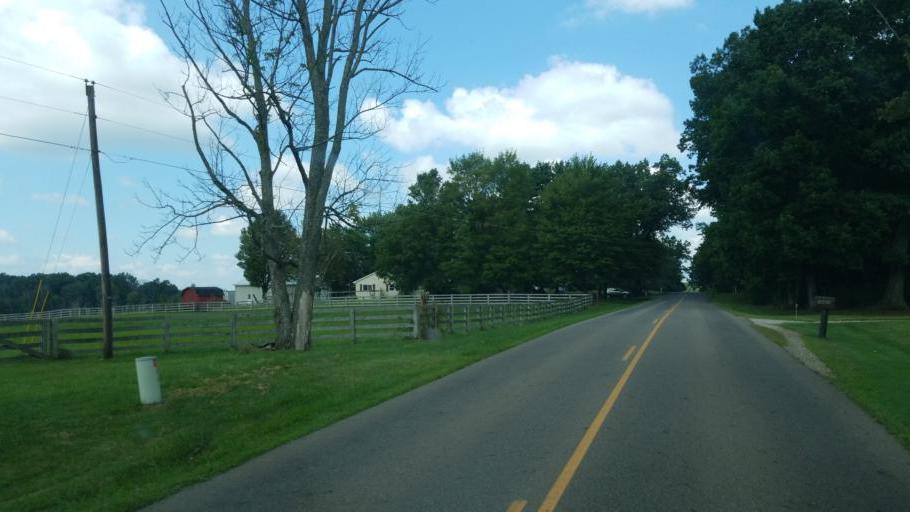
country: US
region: Ohio
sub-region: Knox County
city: Mount Vernon
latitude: 40.4438
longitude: -82.4868
